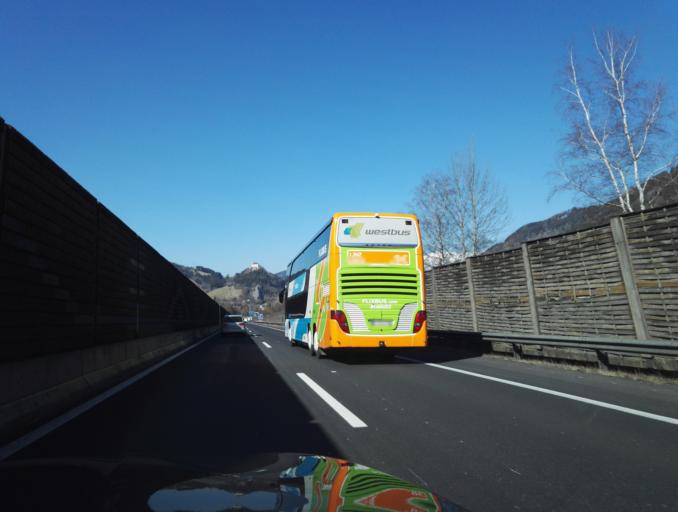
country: AT
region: Styria
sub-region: Politischer Bezirk Liezen
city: Rottenmann
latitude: 47.5228
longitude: 14.3491
